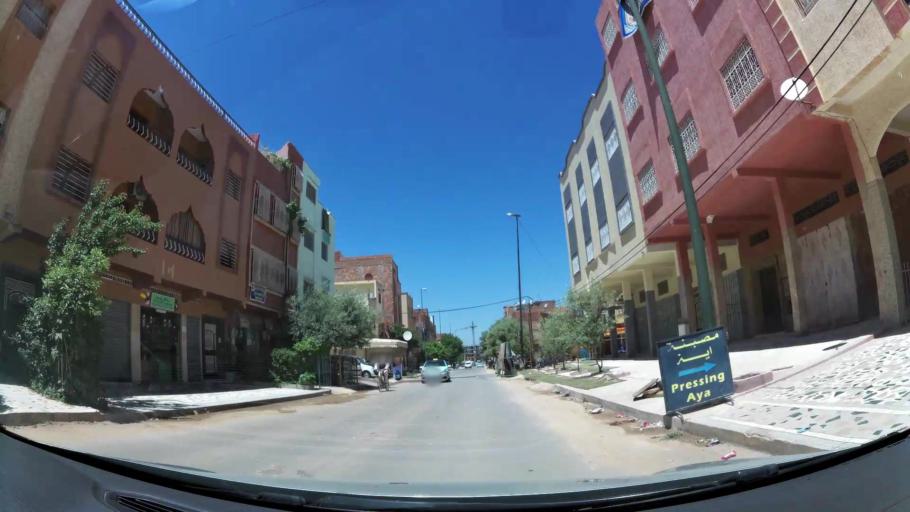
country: MA
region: Meknes-Tafilalet
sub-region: Meknes
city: Meknes
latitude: 33.8661
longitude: -5.5649
